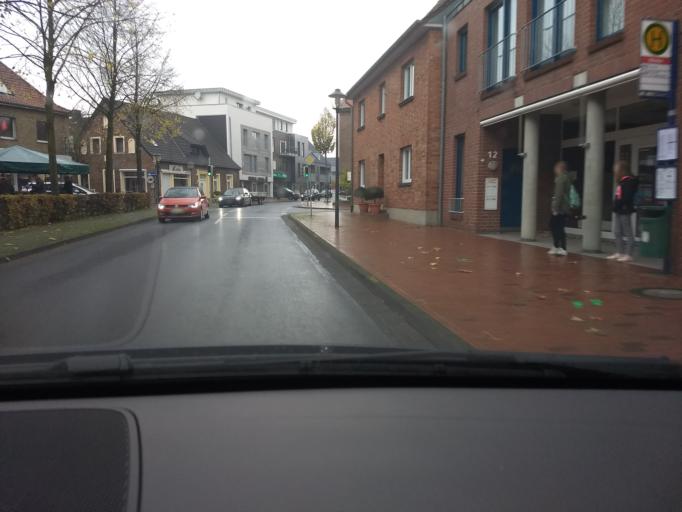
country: DE
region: North Rhine-Westphalia
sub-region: Regierungsbezirk Munster
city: Raesfeld
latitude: 51.7702
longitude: 6.8401
